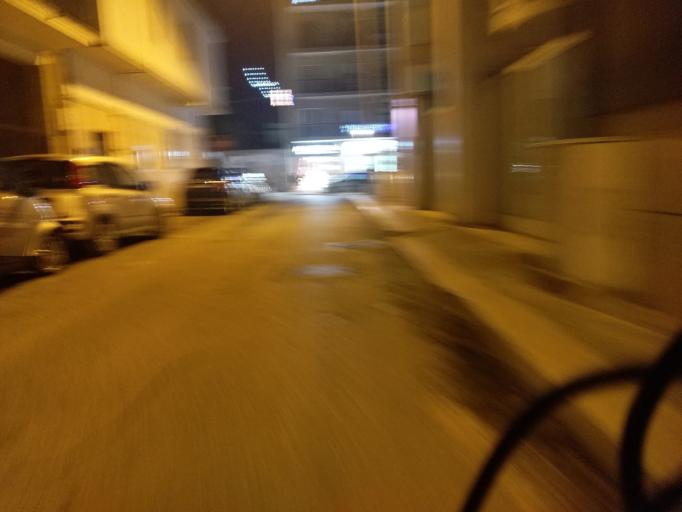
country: IT
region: Apulia
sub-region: Provincia di Bari
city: Modugno
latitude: 41.0863
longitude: 16.7875
